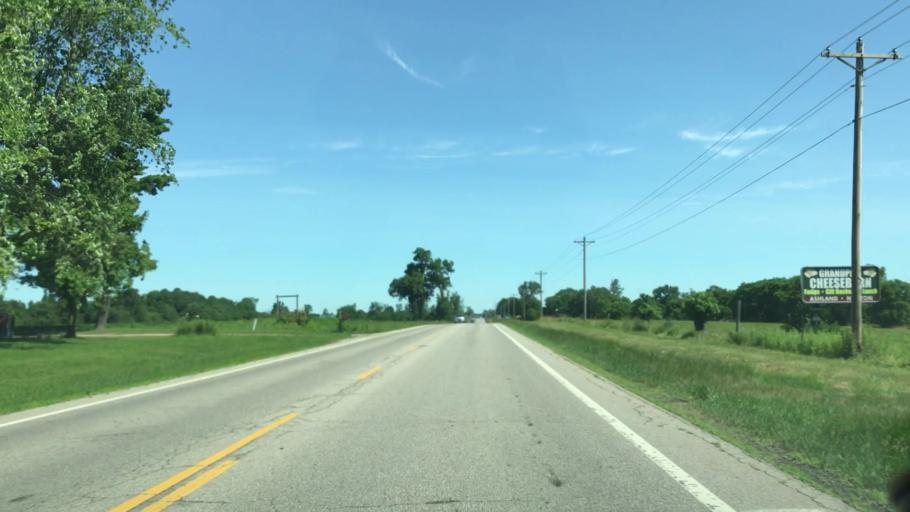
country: US
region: Ohio
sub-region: Huron County
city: Greenwich
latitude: 41.0318
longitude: -82.4854
